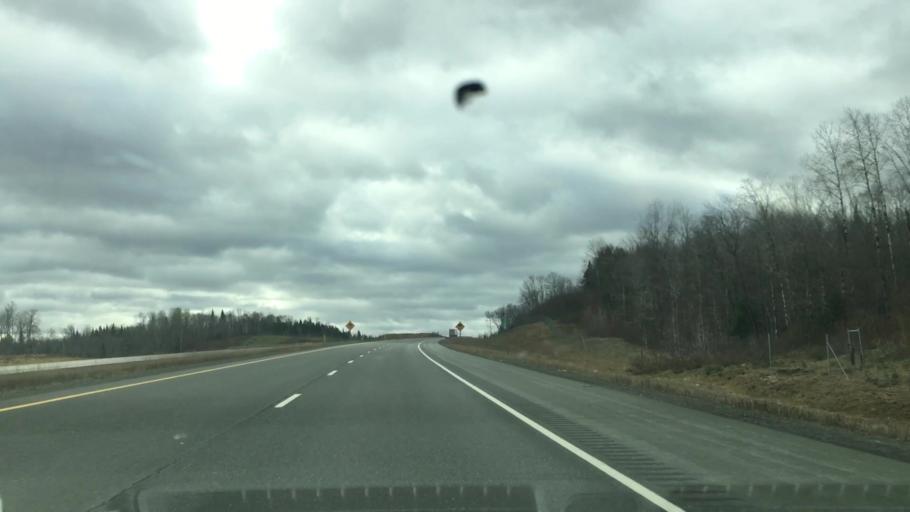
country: US
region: Maine
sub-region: Aroostook County
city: Fort Fairfield
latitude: 46.6633
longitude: -67.7317
